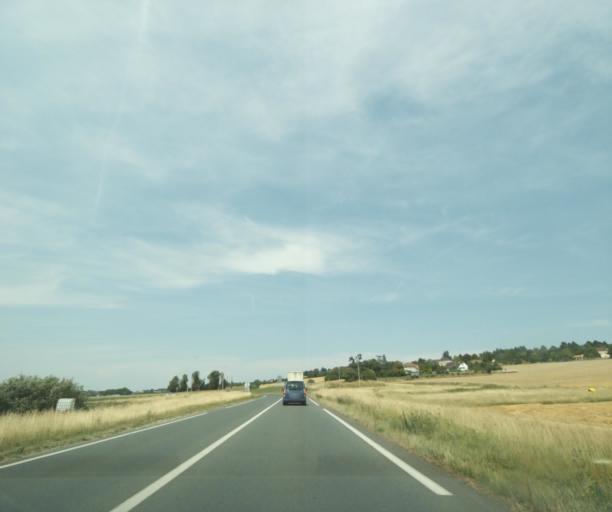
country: FR
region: Poitou-Charentes
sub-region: Departement de la Vienne
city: Chatellerault
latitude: 46.8063
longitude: 0.5654
